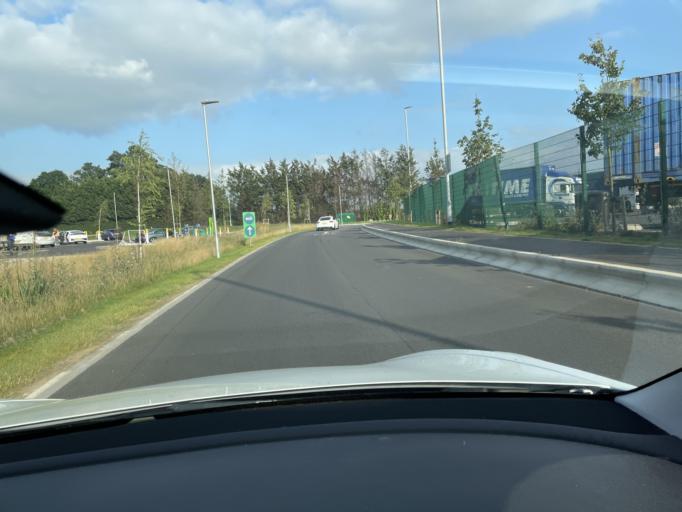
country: GB
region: England
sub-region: Warwickshire
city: Rugby
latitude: 52.4103
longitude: -1.2467
